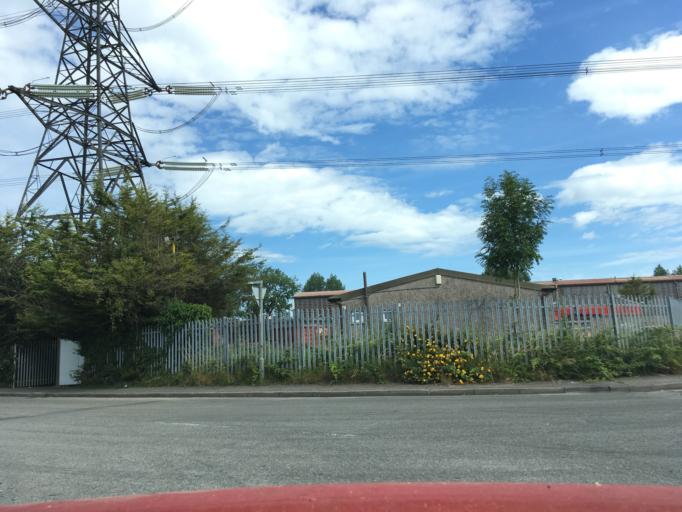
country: GB
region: Wales
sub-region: Newport
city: Newport
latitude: 51.5670
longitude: -2.9777
